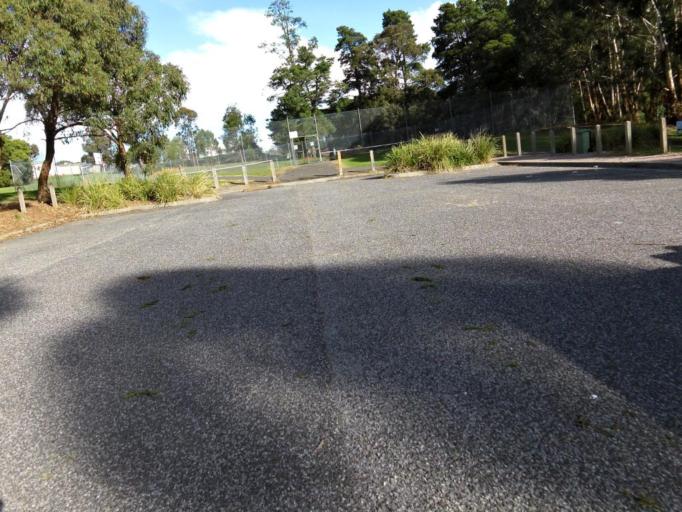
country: AU
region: Victoria
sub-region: Maroondah
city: Croydon Hills
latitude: -37.7741
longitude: 145.2709
